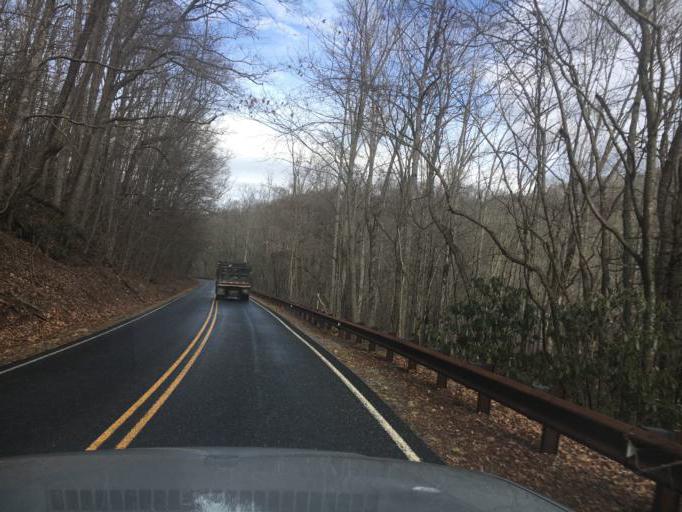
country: US
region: North Carolina
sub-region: Haywood County
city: Canton
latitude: 35.3773
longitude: -82.8091
